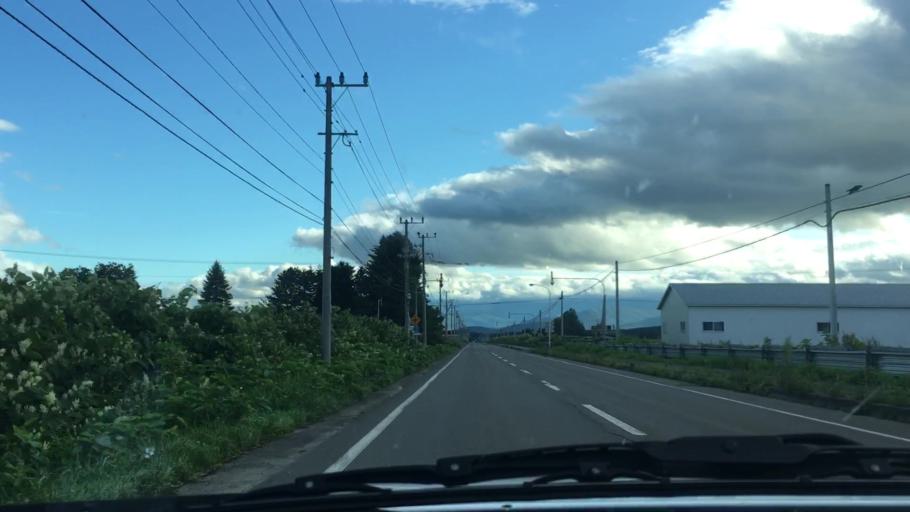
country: JP
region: Hokkaido
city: Otofuke
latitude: 43.1553
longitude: 142.9021
